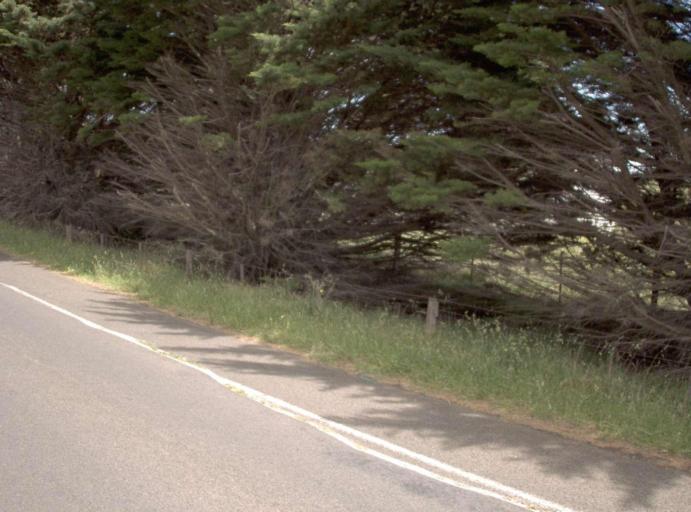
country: AU
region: Victoria
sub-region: Bass Coast
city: Phillip Island
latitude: -38.4967
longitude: 145.2351
